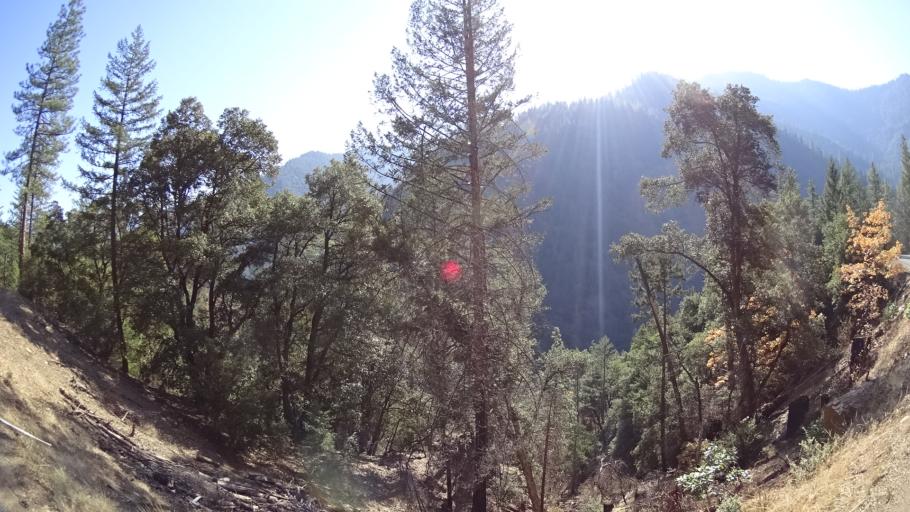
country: US
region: California
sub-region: Siskiyou County
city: Happy Camp
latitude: 41.6990
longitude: -123.0518
